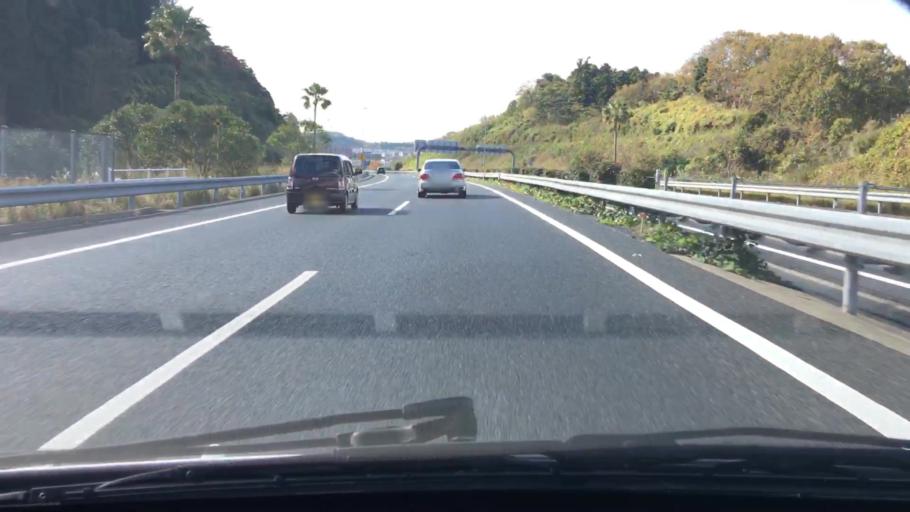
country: JP
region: Chiba
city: Kisarazu
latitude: 35.3539
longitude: 139.9484
